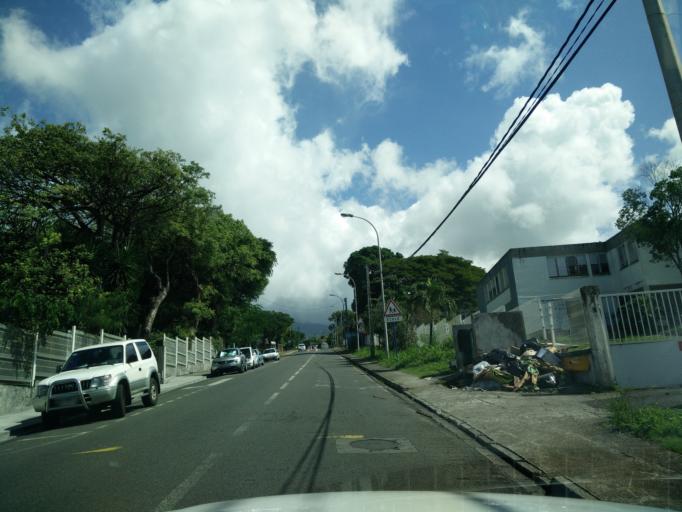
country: GP
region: Guadeloupe
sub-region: Guadeloupe
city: Basse-Terre
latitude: 15.9928
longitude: -61.7201
